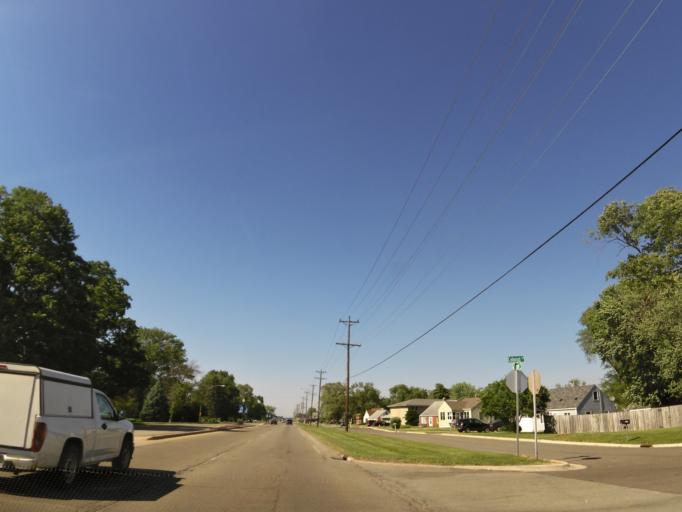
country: US
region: Illinois
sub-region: Winnebago County
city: Loves Park
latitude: 42.3295
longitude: -89.0564
